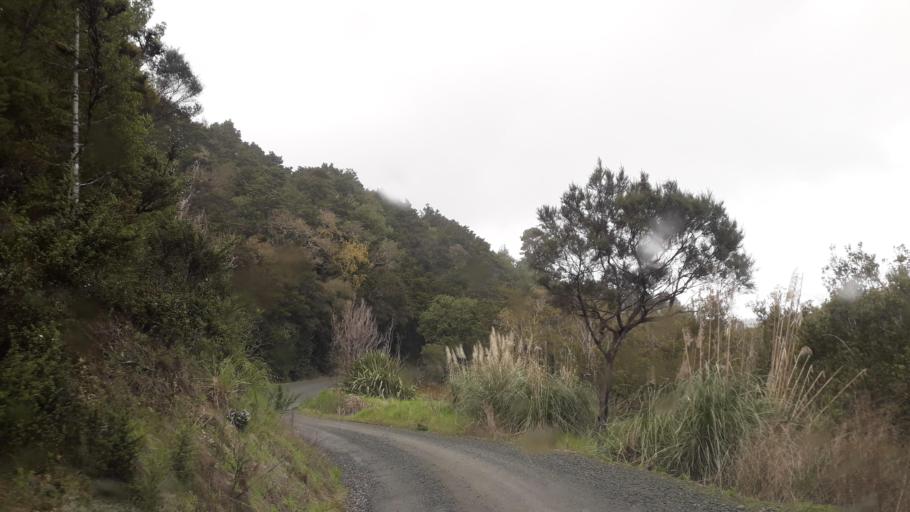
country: NZ
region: Northland
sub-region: Far North District
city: Waimate North
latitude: -35.3067
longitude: 173.5635
